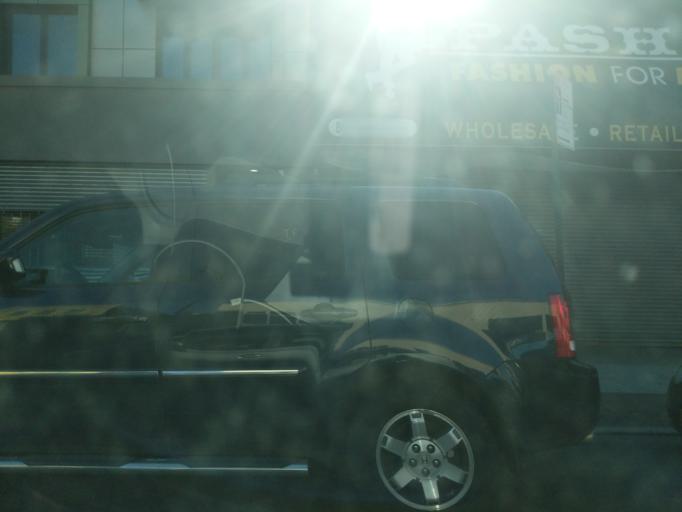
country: US
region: New York
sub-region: Kings County
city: Brooklyn
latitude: 40.6517
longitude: -73.9592
